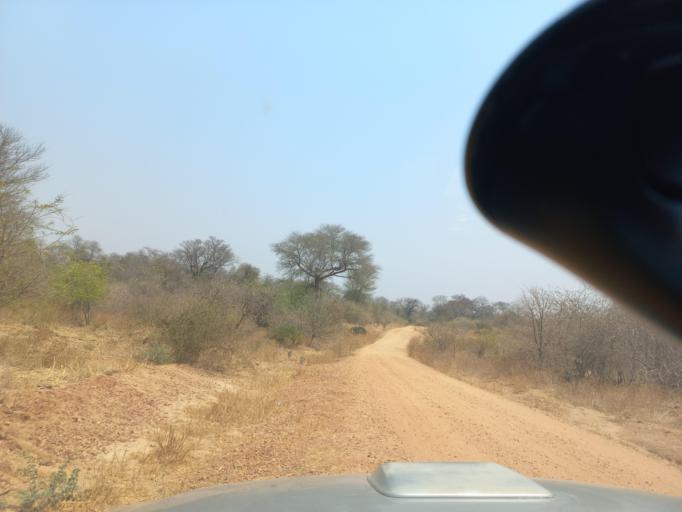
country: ZW
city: Chirundu
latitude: -15.9418
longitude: 28.8213
